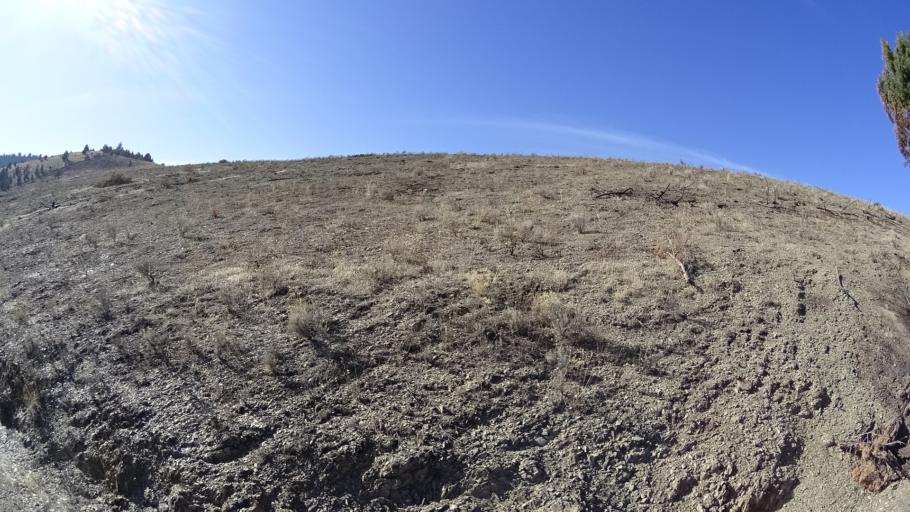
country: US
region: California
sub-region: Siskiyou County
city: Montague
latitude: 41.6349
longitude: -122.5403
